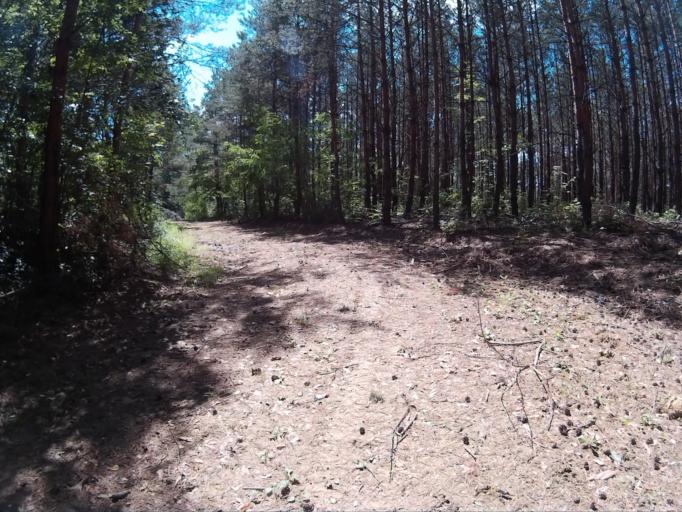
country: HU
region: Zala
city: Zalalovo
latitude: 46.8149
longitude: 16.6018
